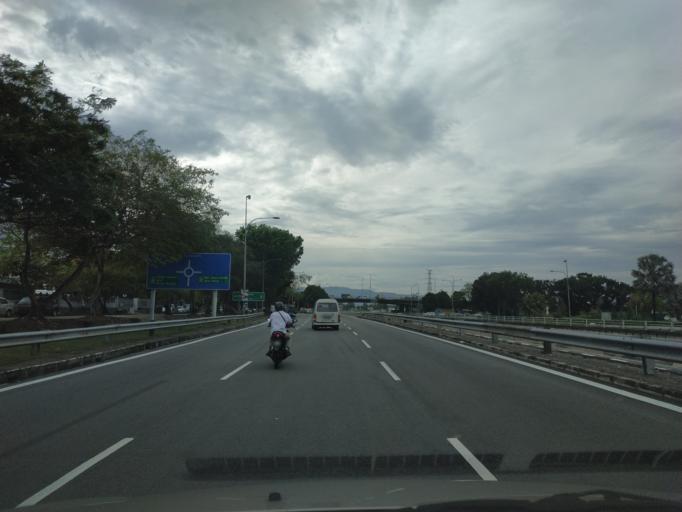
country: MY
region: Penang
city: Perai
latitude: 5.3990
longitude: 100.4086
